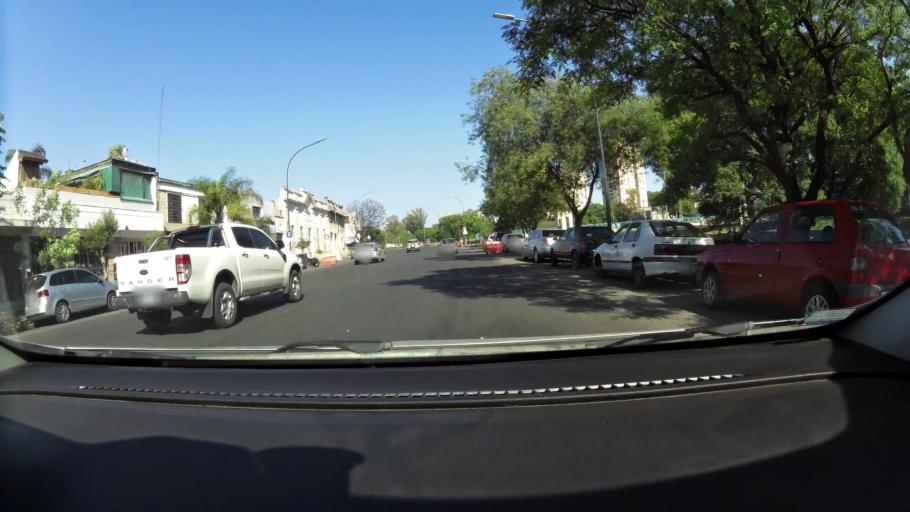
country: AR
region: Cordoba
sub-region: Departamento de Capital
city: Cordoba
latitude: -31.4065
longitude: -64.1791
